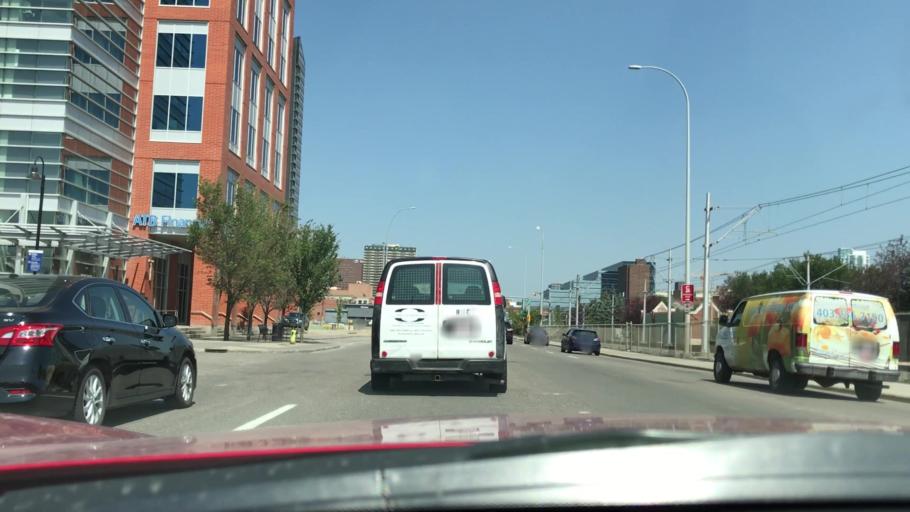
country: CA
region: Alberta
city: Calgary
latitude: 51.0393
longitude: -114.0586
